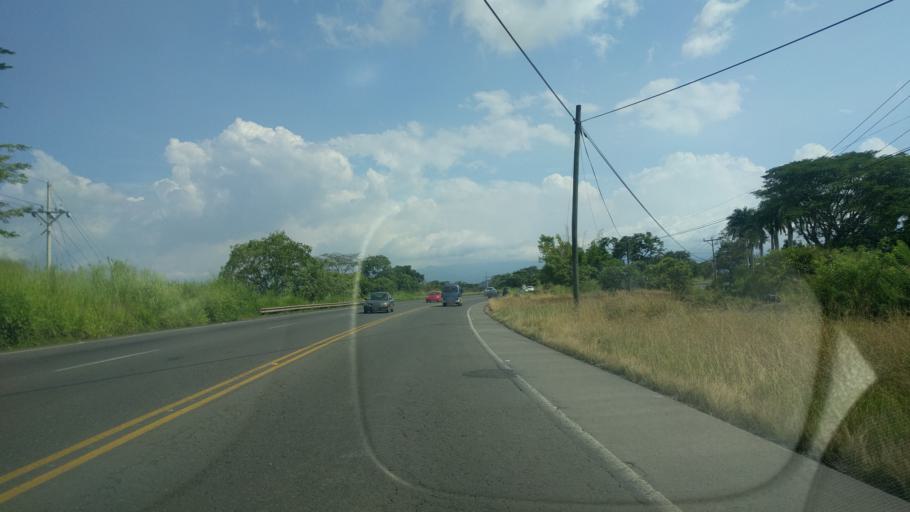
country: CR
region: Alajuela
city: Atenas
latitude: 10.0366
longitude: -84.3606
